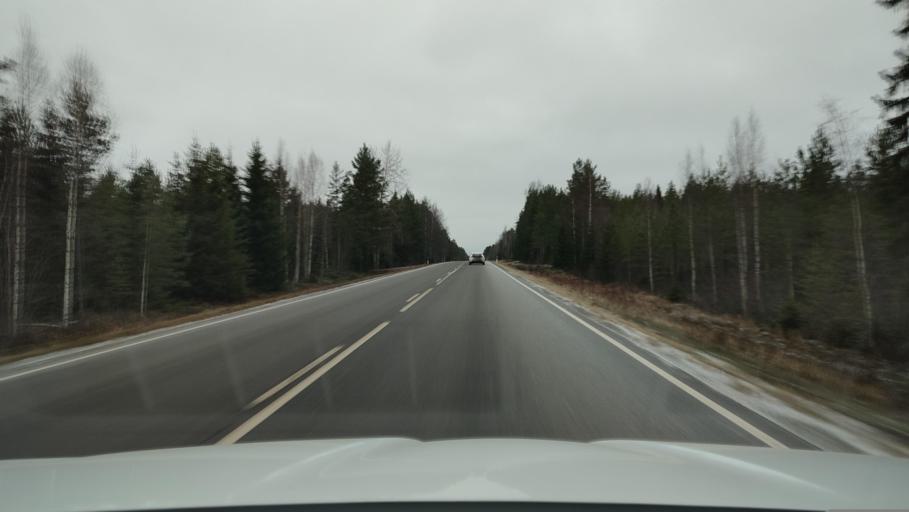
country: FI
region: Ostrobothnia
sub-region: Sydosterbotten
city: Naerpes
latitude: 62.5756
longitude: 21.4903
